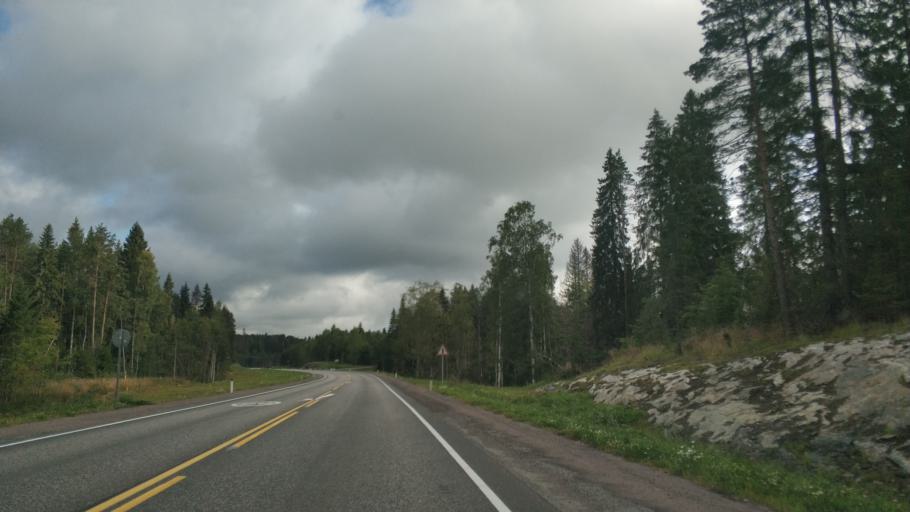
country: RU
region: Republic of Karelia
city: Khelyulya
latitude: 61.8044
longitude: 30.6186
